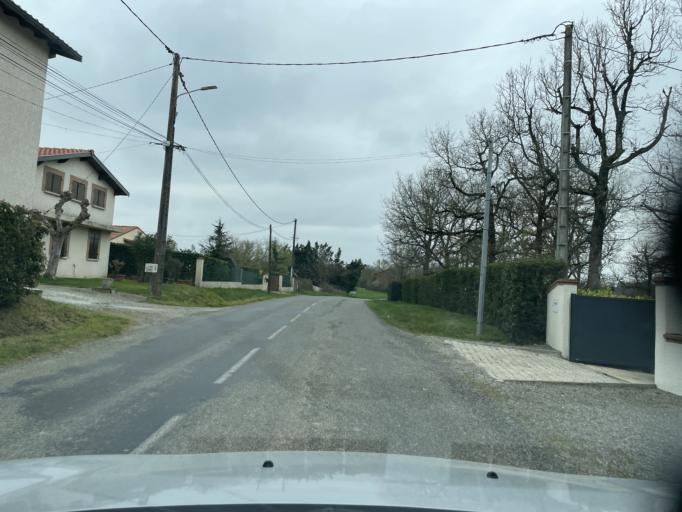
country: FR
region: Midi-Pyrenees
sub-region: Departement du Gers
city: Pujaudran
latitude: 43.6068
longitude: 1.1598
